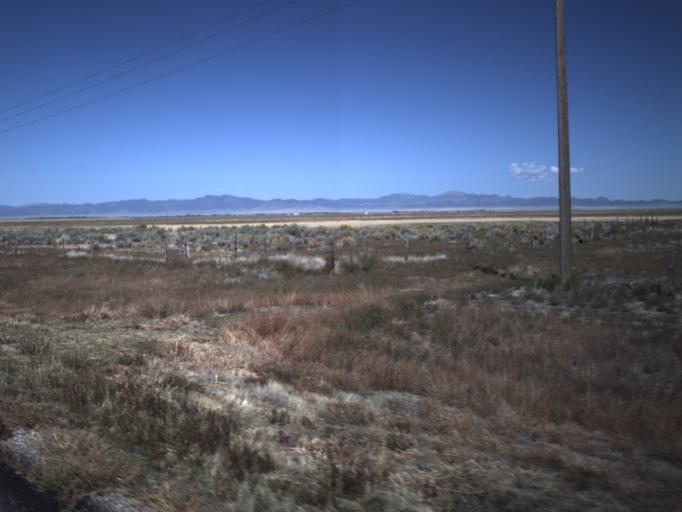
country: US
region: Utah
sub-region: Washington County
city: Enterprise
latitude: 37.6792
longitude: -113.5720
